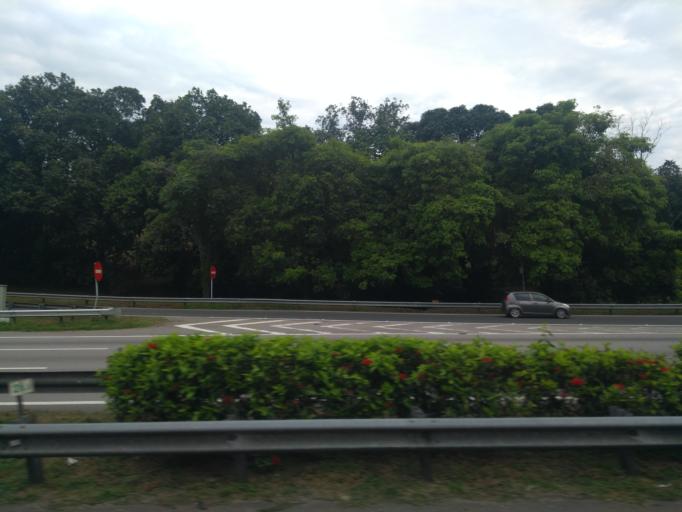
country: MY
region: Melaka
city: Pulau Sebang
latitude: 2.4445
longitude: 102.1882
